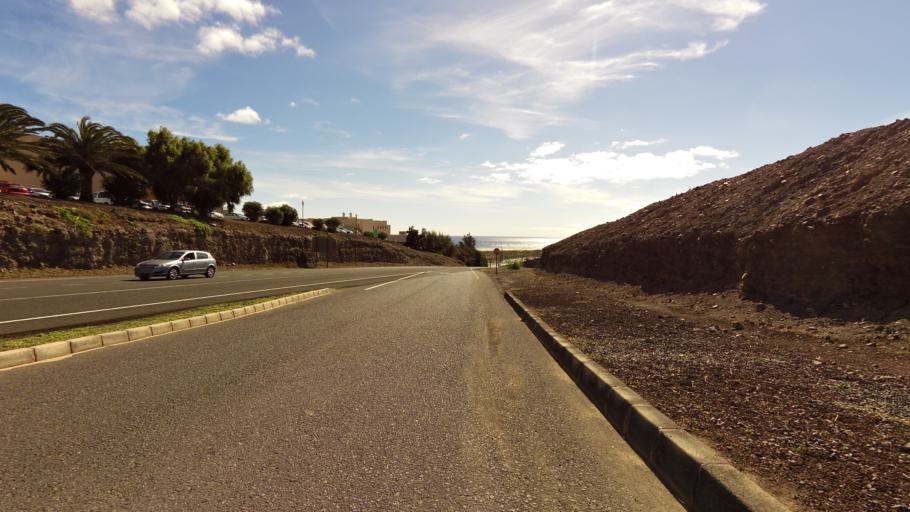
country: ES
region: Canary Islands
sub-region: Provincia de Las Palmas
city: Pajara
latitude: 28.0584
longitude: -14.3211
